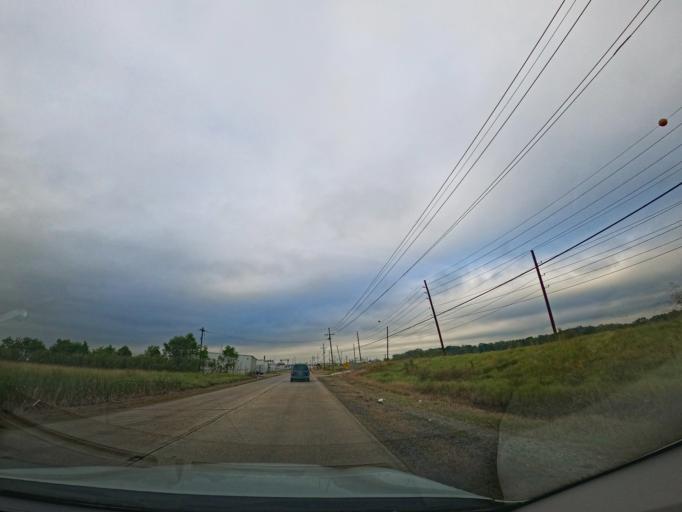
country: US
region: Louisiana
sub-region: Terrebonne Parish
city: Houma
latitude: 29.5733
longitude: -90.7029
